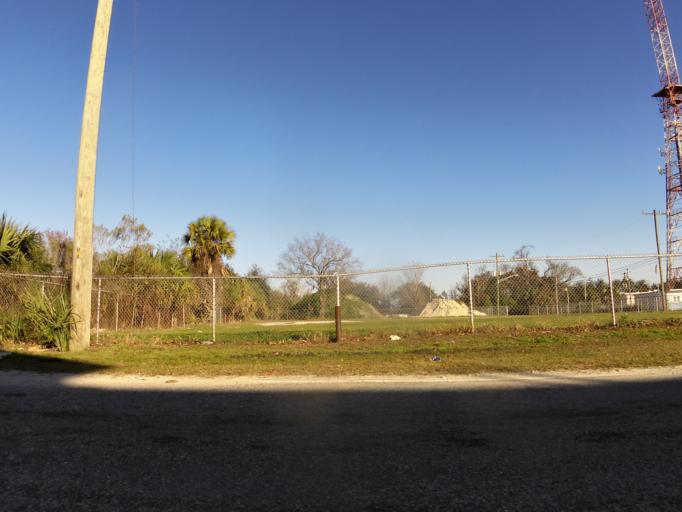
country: US
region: Florida
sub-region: Duval County
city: Jacksonville
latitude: 30.3315
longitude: -81.6968
